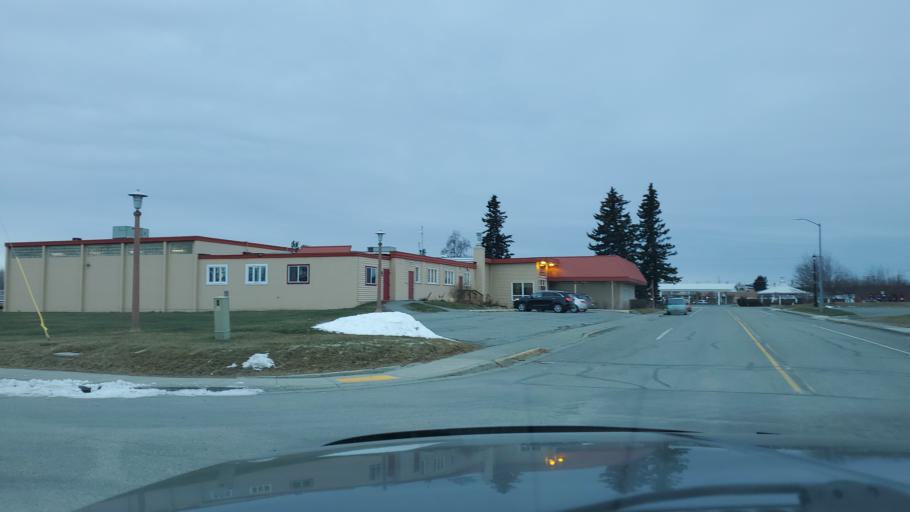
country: US
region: Alaska
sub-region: Matanuska-Susitna Borough
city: Palmer
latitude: 61.5988
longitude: -149.1106
